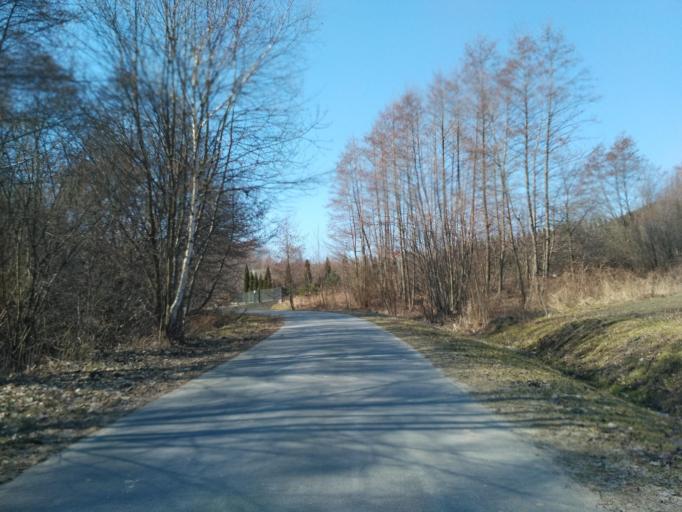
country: PL
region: Subcarpathian Voivodeship
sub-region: Powiat rzeszowski
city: Niechobrz
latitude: 49.9712
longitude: 21.8818
